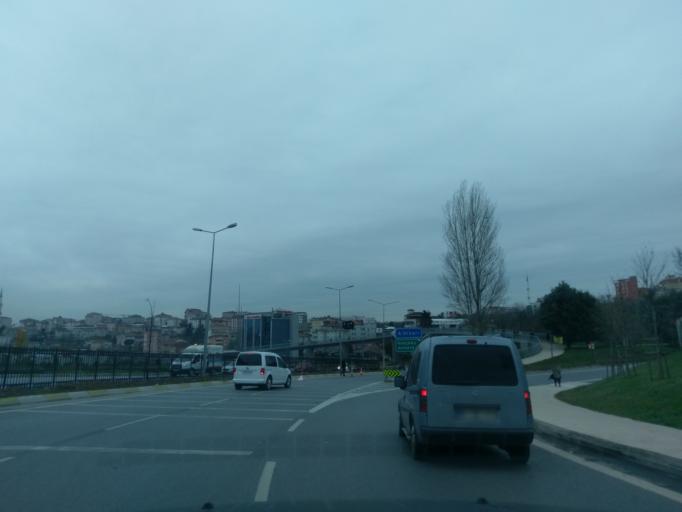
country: TR
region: Istanbul
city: Umraniye
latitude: 41.0884
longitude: 29.0897
